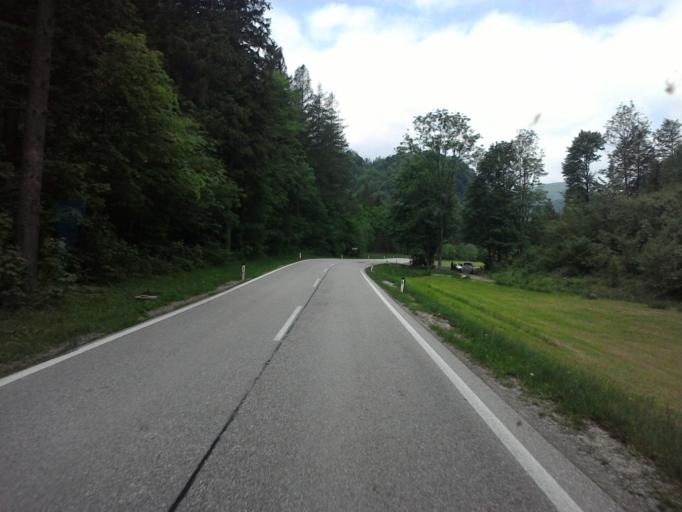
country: AT
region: Upper Austria
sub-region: Politischer Bezirk Steyr-Land
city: Weyer
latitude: 47.8625
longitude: 14.6117
